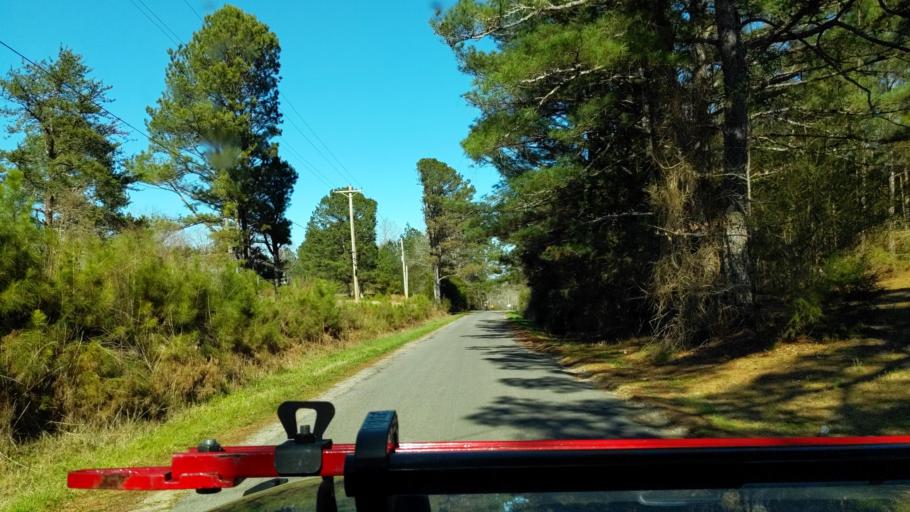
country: US
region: Alabama
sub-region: Walker County
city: Jasper
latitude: 34.0536
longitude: -87.1525
